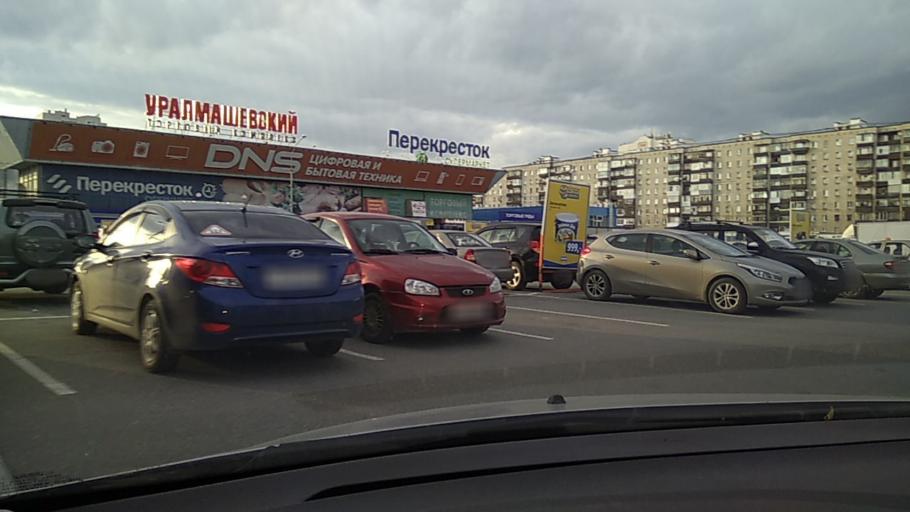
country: RU
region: Sverdlovsk
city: Yekaterinburg
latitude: 56.9012
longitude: 60.5893
